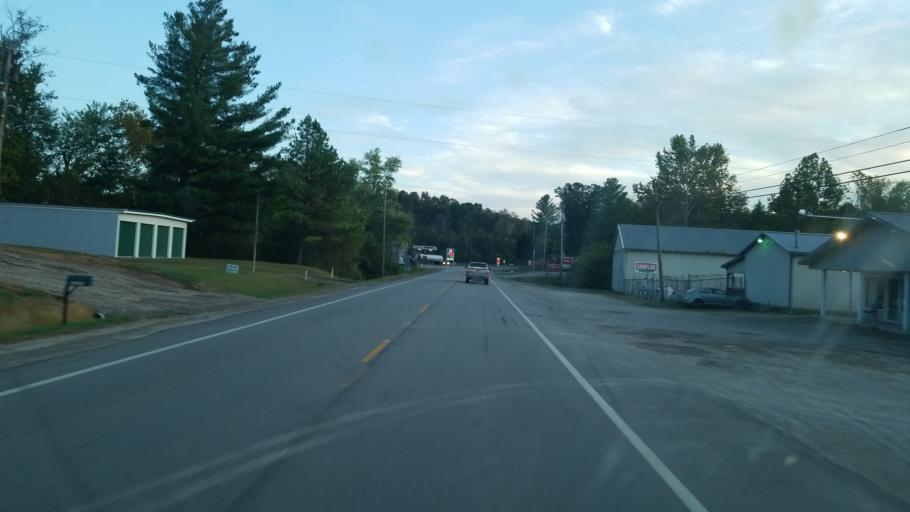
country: US
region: West Virginia
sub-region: Mason County
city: New Haven
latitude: 39.0888
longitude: -81.9259
